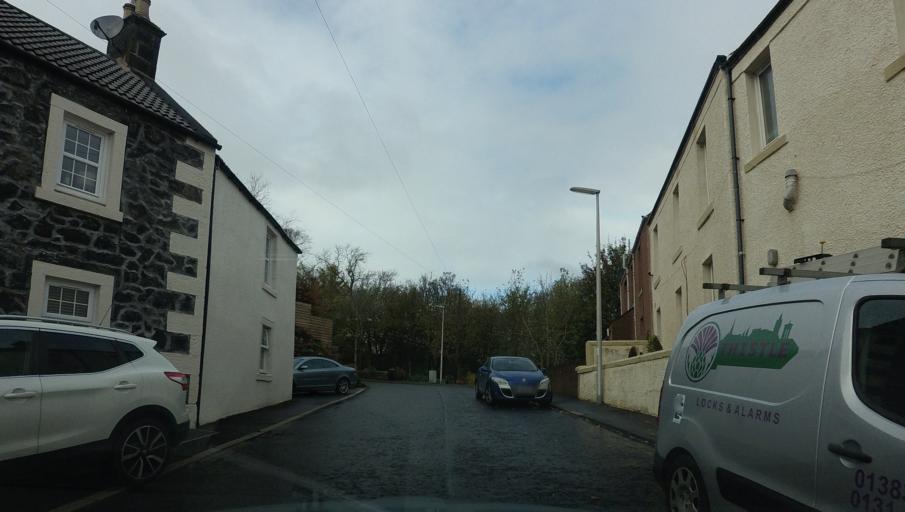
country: GB
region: Scotland
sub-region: Fife
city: East Wemyss
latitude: 56.1591
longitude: -3.0656
